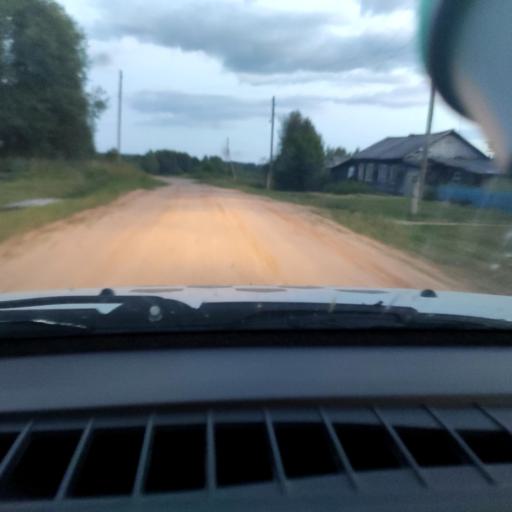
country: RU
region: Kirov
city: Darovskoy
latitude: 58.9907
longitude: 47.8677
